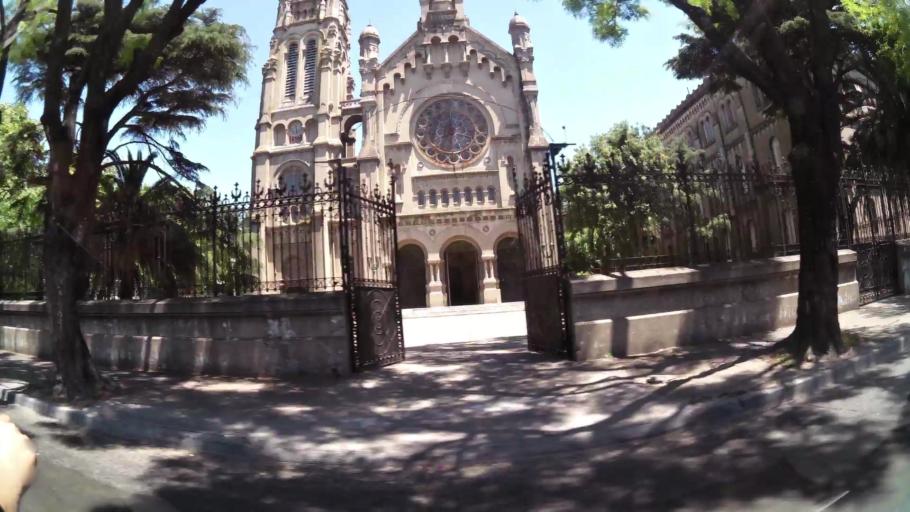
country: AR
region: Buenos Aires
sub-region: Partido de Avellaneda
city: Avellaneda
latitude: -34.6508
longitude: -58.3891
